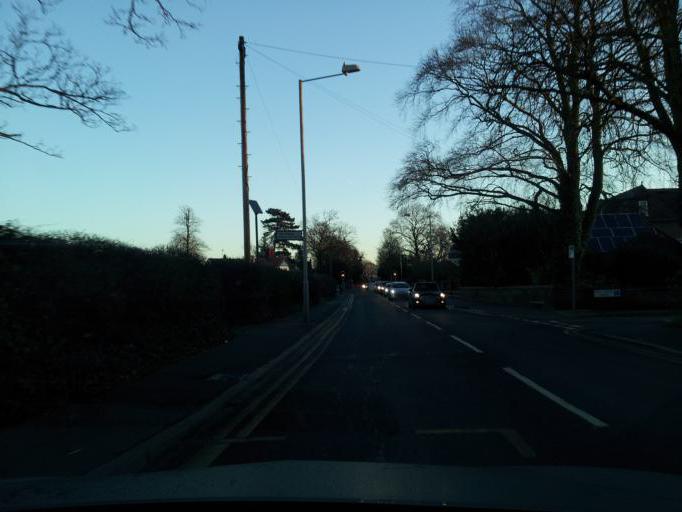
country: GB
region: England
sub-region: Essex
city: Chelmsford
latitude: 51.7393
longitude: 0.4885
